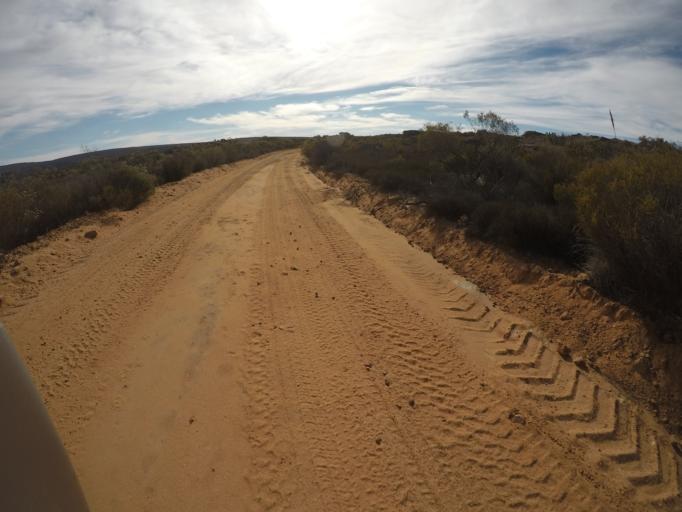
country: ZA
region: Western Cape
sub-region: West Coast District Municipality
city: Vredendal
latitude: -31.7475
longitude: 18.8235
